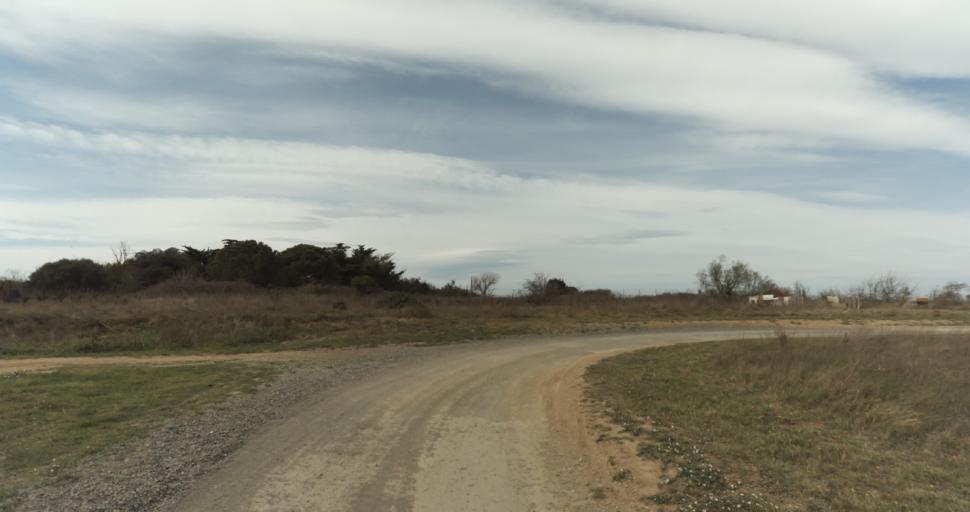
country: FR
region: Languedoc-Roussillon
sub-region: Departement de l'Herault
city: Marseillan
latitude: 43.3401
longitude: 3.5280
